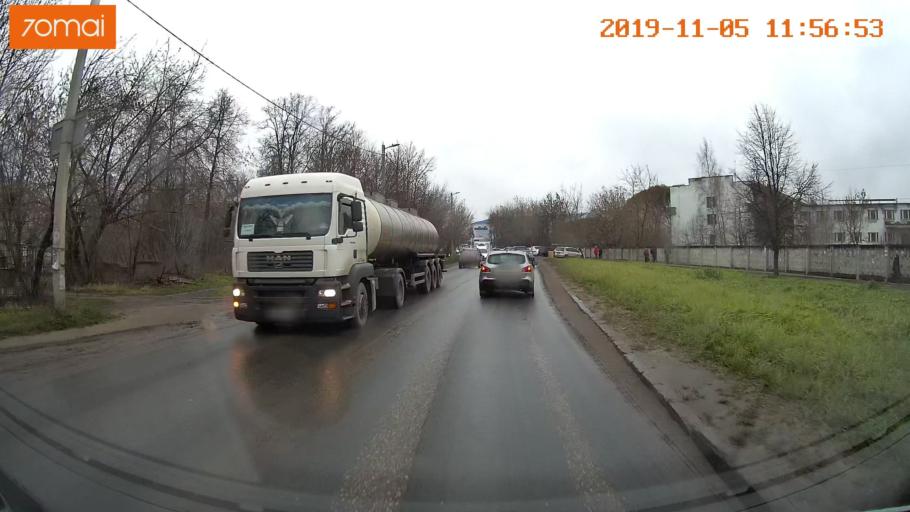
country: RU
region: Ivanovo
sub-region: Gorod Ivanovo
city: Ivanovo
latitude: 56.9851
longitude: 41.0329
